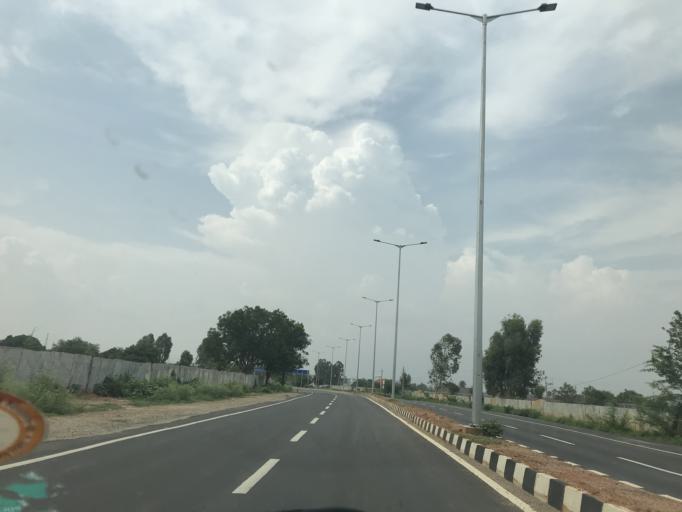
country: IN
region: Karnataka
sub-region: Bangalore Urban
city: Yelahanka
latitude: 13.1159
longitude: 77.6682
